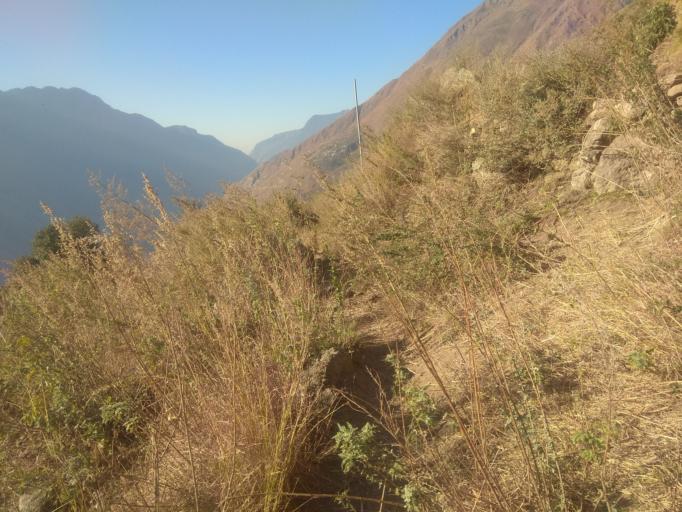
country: NP
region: Mid Western
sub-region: Bheri Zone
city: Dailekh
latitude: 29.2876
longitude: 81.7131
